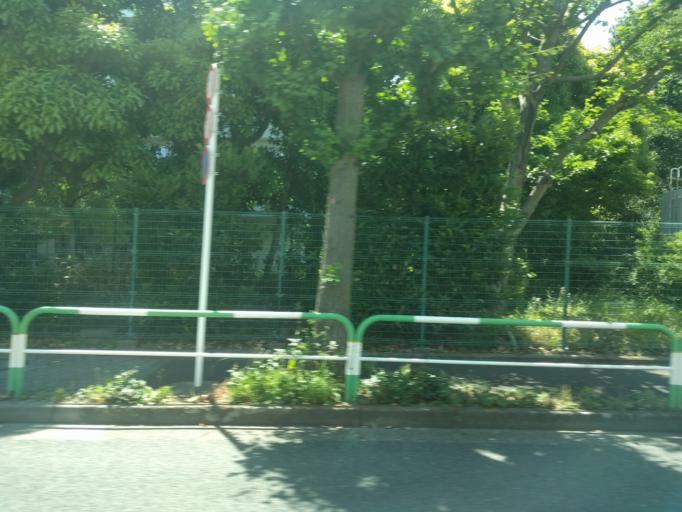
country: JP
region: Tokyo
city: Mitaka-shi
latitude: 35.6583
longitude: 139.6205
